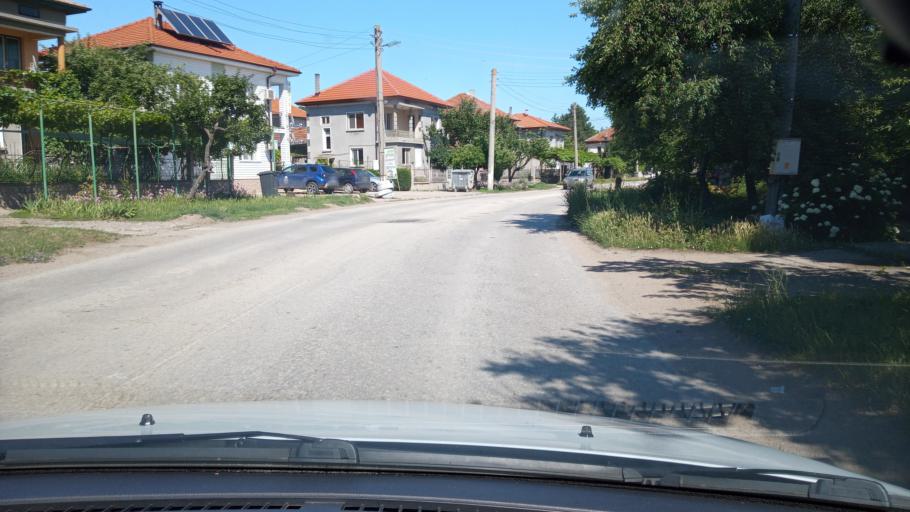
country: BG
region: Pleven
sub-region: Obshtina Dolna Mitropoliya
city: Dolna Mitropoliya
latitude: 43.4485
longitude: 24.5716
